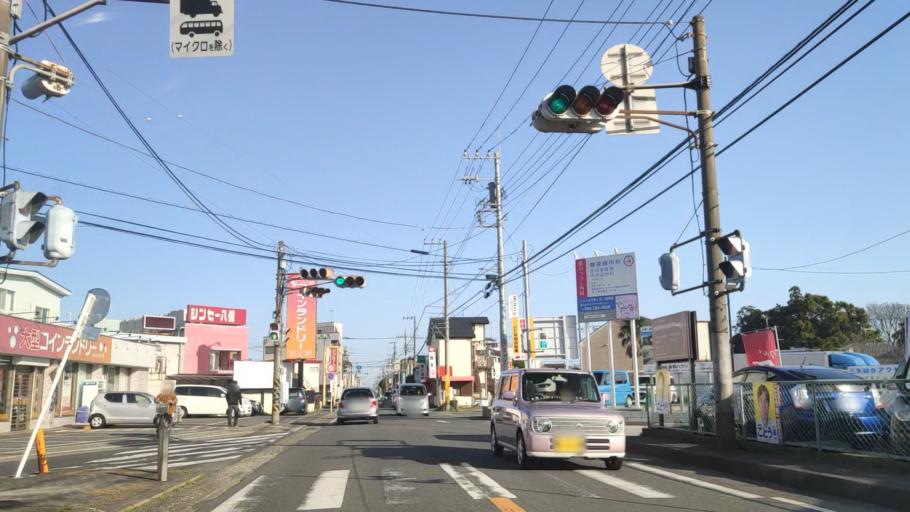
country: JP
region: Kanagawa
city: Zama
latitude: 35.5042
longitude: 139.3508
